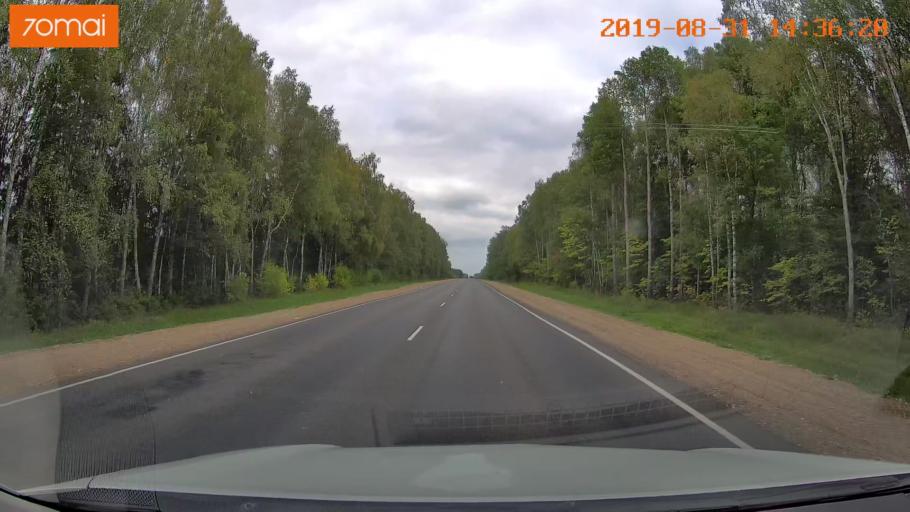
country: RU
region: Smolensk
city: Yekimovichi
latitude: 54.1693
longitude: 33.4773
